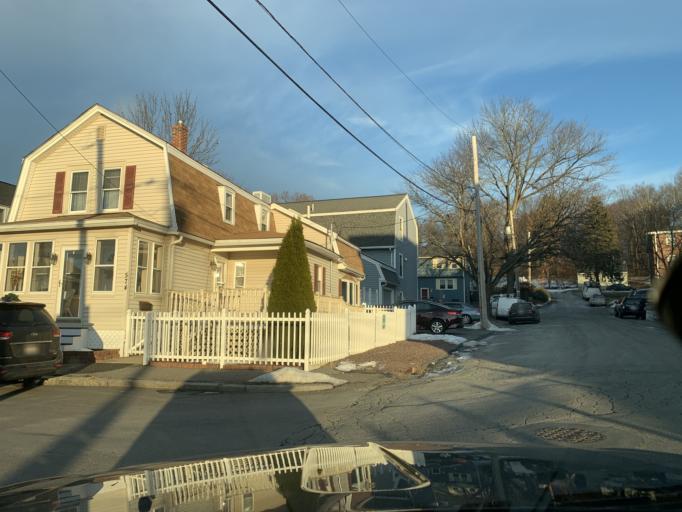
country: US
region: Massachusetts
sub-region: Middlesex County
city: Lowell
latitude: 42.6341
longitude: -71.2988
